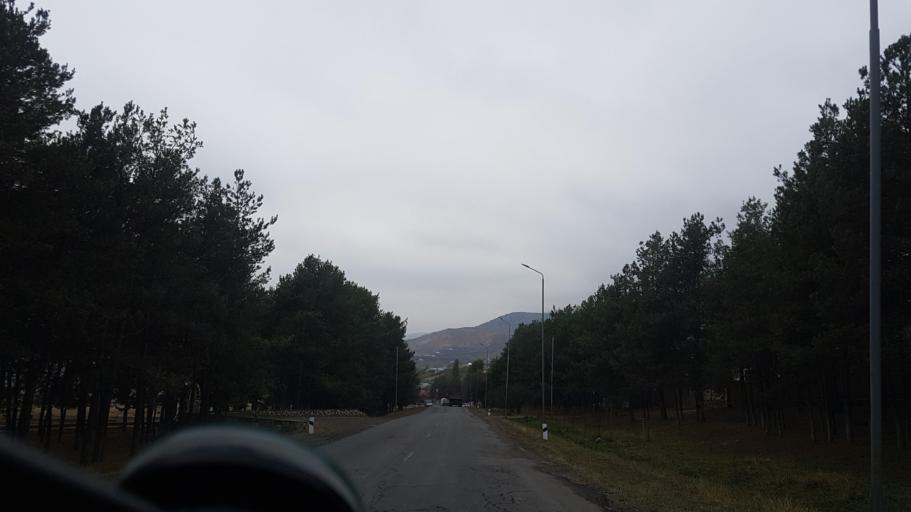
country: AZ
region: Gadabay Rayon
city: Ariqdam
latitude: 40.6028
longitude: 45.8117
